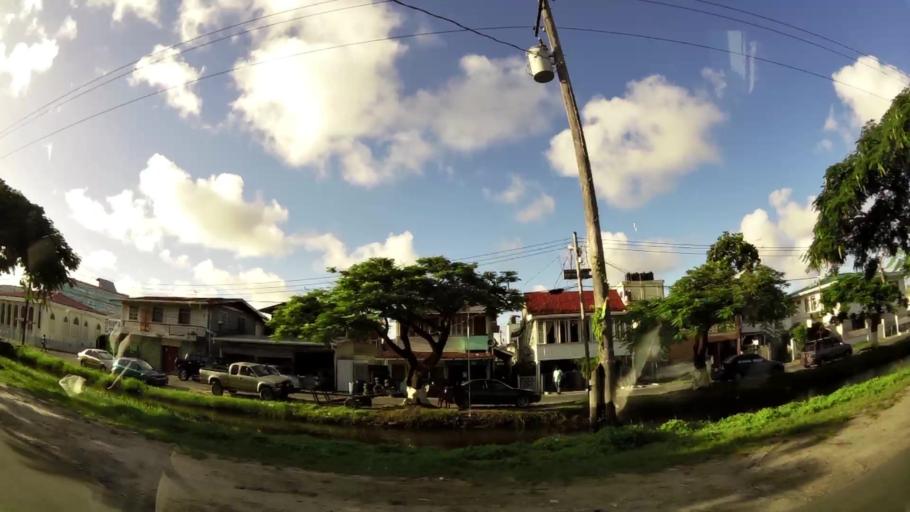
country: GY
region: Demerara-Mahaica
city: Georgetown
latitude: 6.8080
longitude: -58.1595
